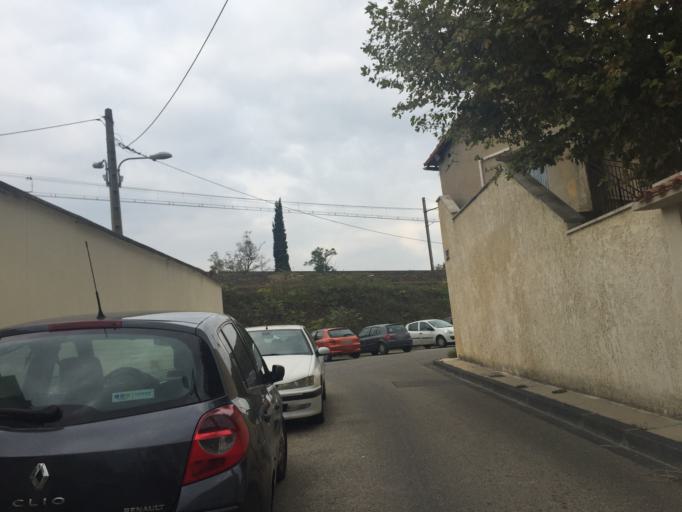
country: FR
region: Provence-Alpes-Cote d'Azur
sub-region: Departement du Vaucluse
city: Avignon
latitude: 43.9523
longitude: 4.8245
